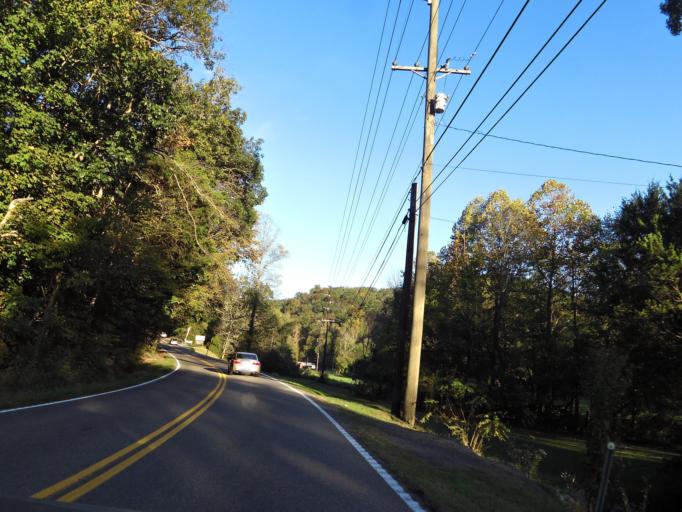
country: US
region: Tennessee
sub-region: Sevier County
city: Pigeon Forge
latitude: 35.6885
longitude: -83.7166
